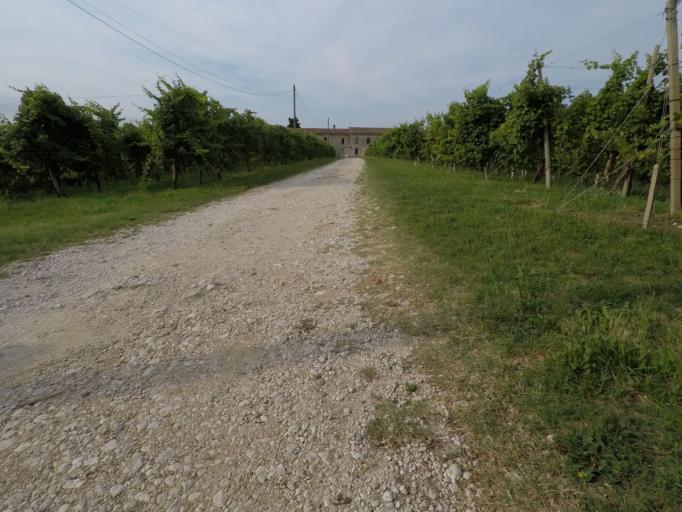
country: IT
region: Veneto
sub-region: Provincia di Treviso
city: Cordignano
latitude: 45.9709
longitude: 12.4197
